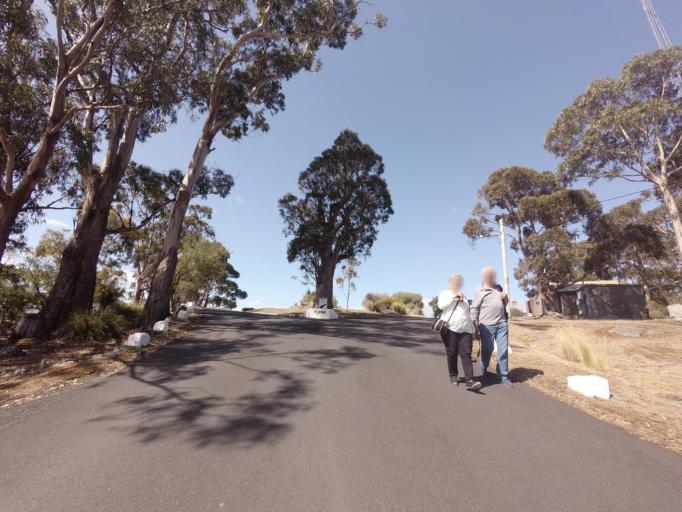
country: AU
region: Tasmania
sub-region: Kingborough
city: Taroona
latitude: -42.9244
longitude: 147.3433
